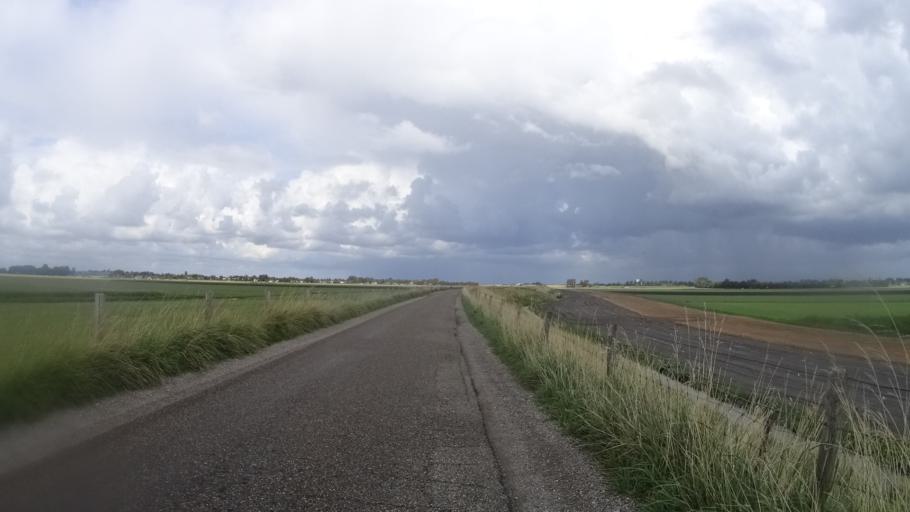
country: NL
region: North Holland
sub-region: Gemeente Schagen
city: Schagen
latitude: 52.7865
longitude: 4.7496
